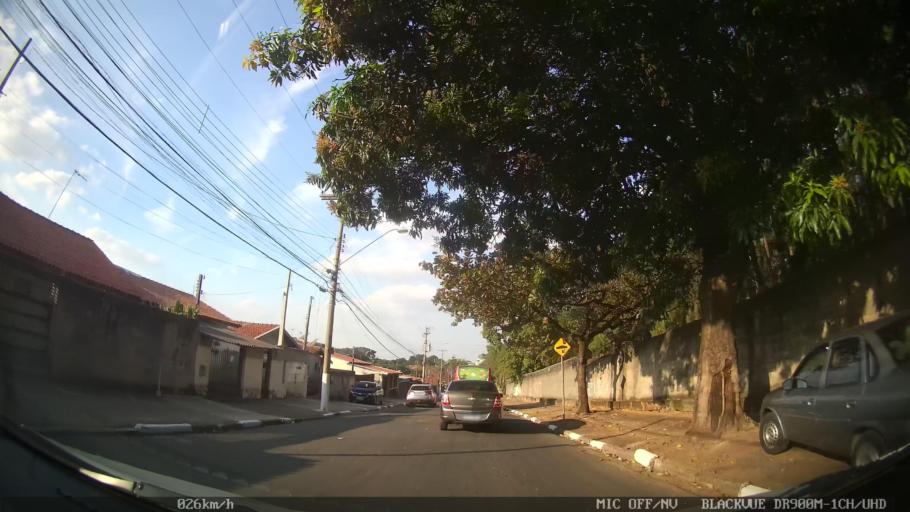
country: BR
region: Sao Paulo
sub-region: Hortolandia
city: Hortolandia
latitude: -22.8754
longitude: -47.1501
